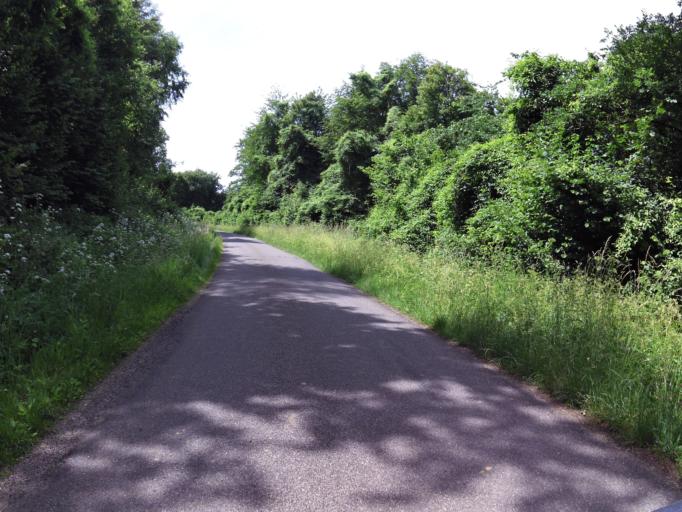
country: FR
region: Lorraine
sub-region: Departement de la Meuse
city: Stenay
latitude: 49.5404
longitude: 5.1344
